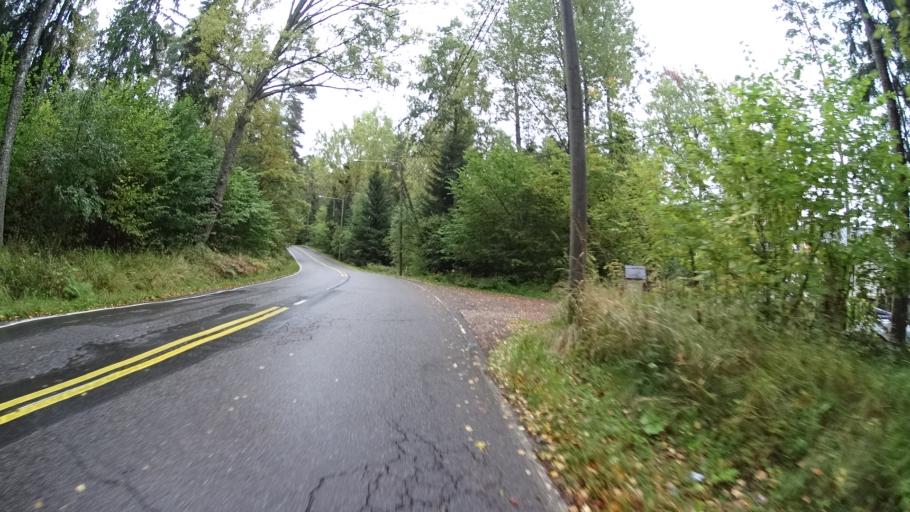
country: FI
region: Uusimaa
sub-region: Helsinki
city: Espoo
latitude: 60.2600
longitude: 24.6528
